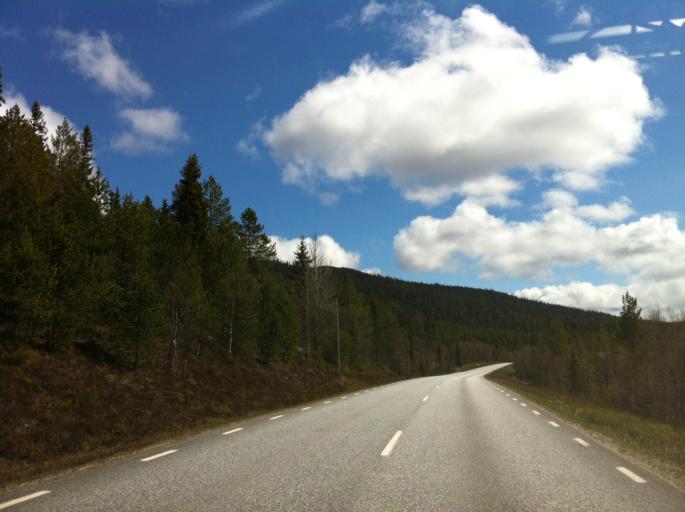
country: SE
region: Jaemtland
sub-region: Are Kommun
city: Are
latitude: 62.5964
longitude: 12.5354
